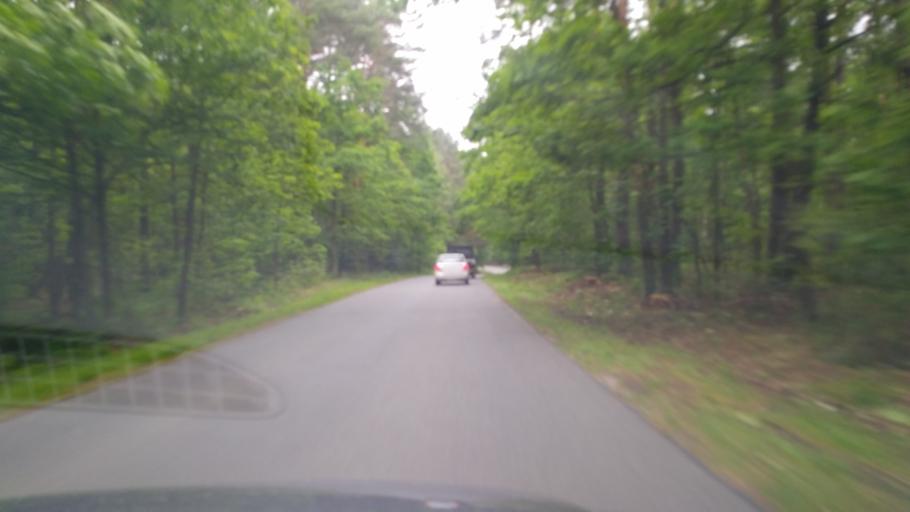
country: PL
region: Subcarpathian Voivodeship
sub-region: Powiat kolbuszowski
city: Niwiska
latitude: 50.1767
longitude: 21.6630
